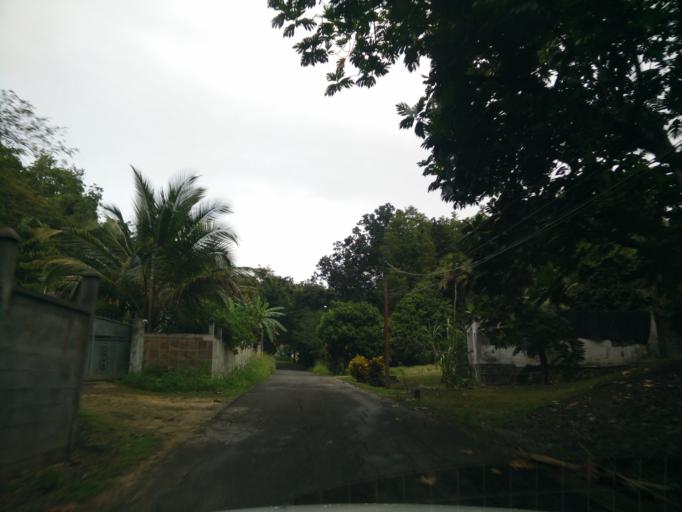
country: GP
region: Guadeloupe
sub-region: Guadeloupe
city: Le Gosier
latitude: 16.2275
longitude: -61.4950
